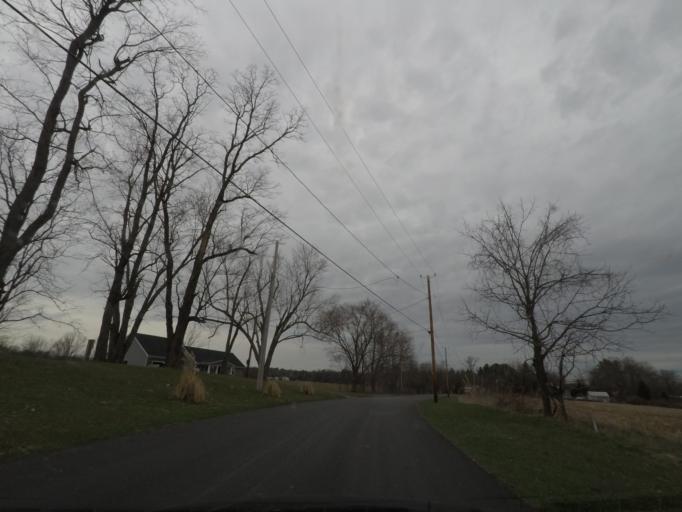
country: US
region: New York
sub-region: Rensselaer County
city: Castleton-on-Hudson
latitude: 42.5593
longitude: -73.7931
